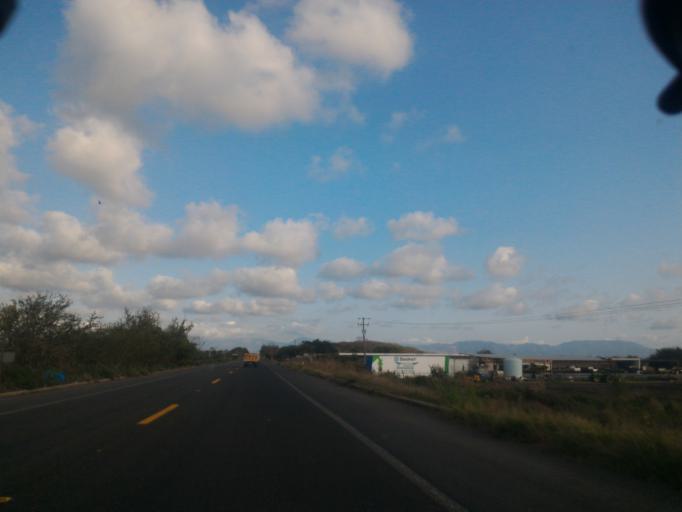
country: MX
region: Michoacan
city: Coahuayana Viejo
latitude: 18.7848
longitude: -103.7761
